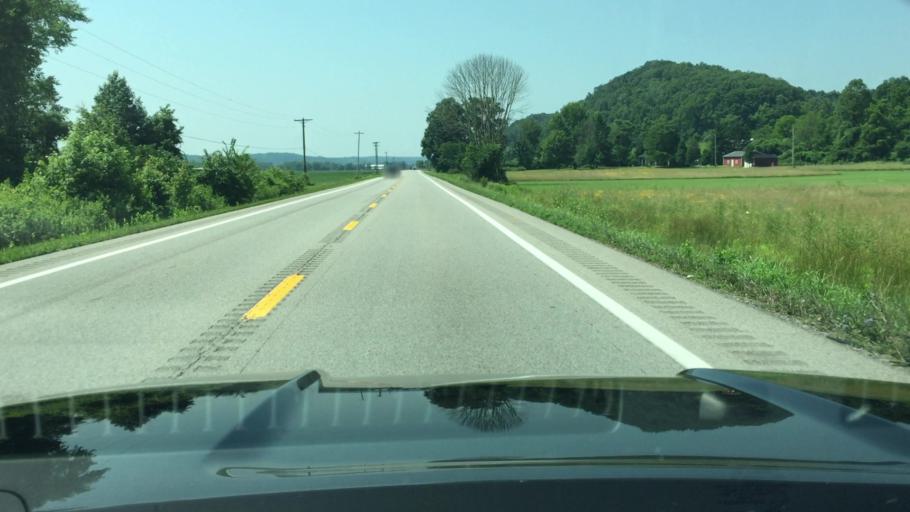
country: US
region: West Virginia
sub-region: Putnam County
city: Buffalo
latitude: 38.6737
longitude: -81.9662
